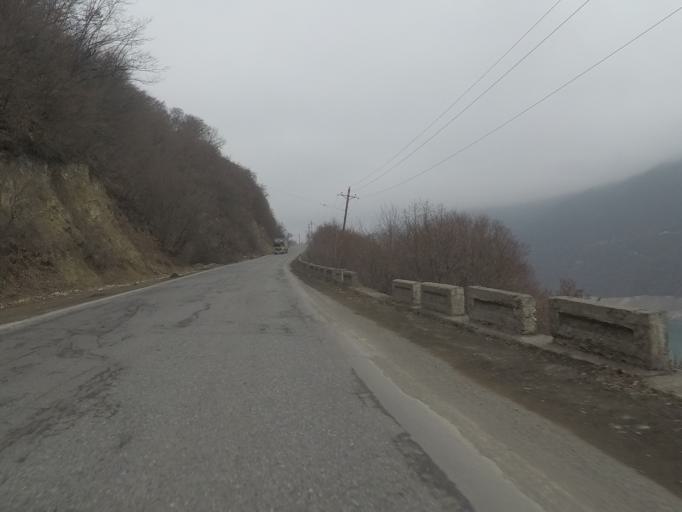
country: GE
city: Zhinvali
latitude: 42.1496
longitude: 44.7606
